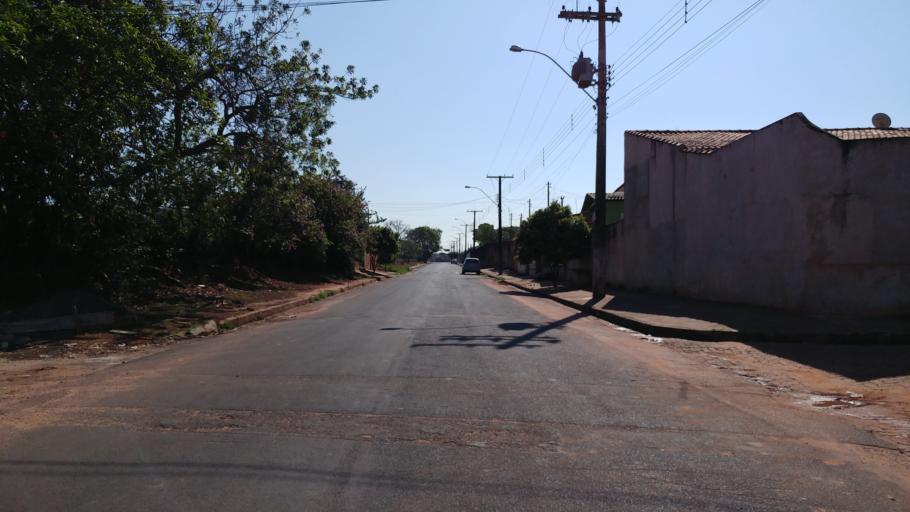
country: BR
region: Sao Paulo
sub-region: Paraguacu Paulista
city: Paraguacu Paulista
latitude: -22.4067
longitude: -50.5675
